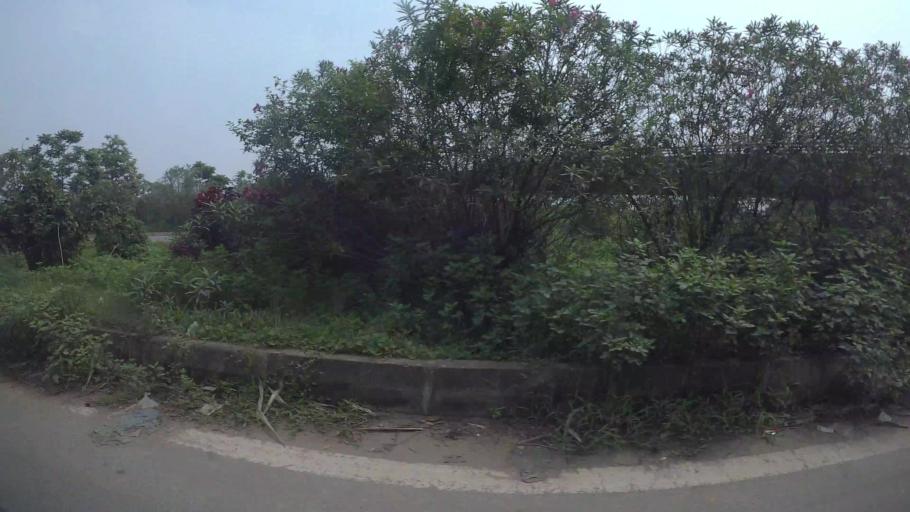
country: VN
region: Ha Noi
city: Lien Quan
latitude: 20.9895
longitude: 105.5362
